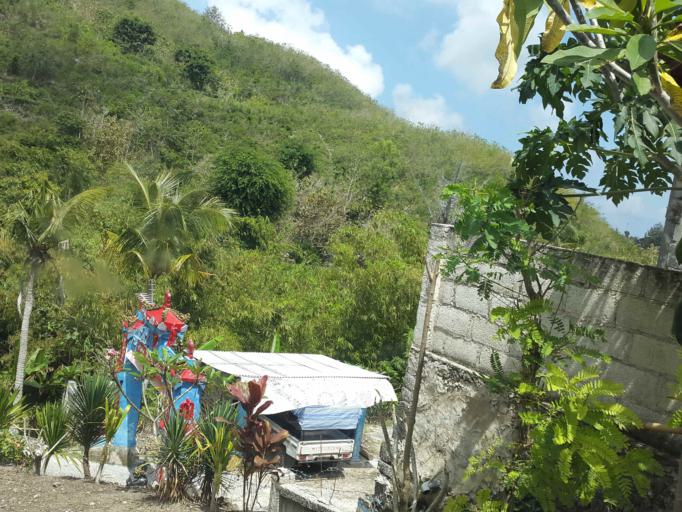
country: ID
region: Bali
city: Klumbu
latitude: -8.7271
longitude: 115.5277
